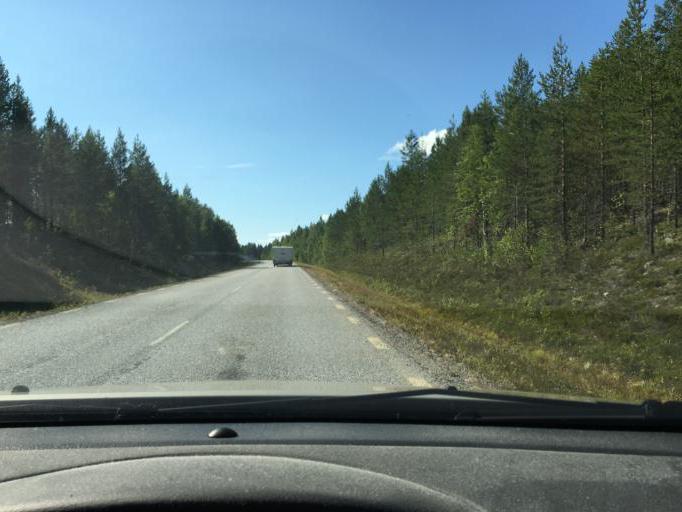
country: SE
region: Norrbotten
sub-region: Lulea Kommun
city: Ranea
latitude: 66.0483
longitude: 22.2621
